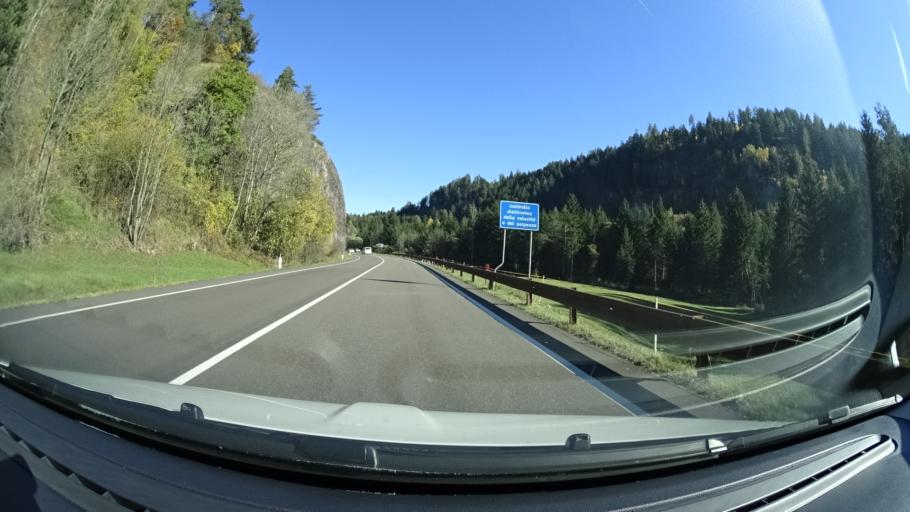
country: IT
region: Trentino-Alto Adige
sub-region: Provincia di Trento
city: Cavalese
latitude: 46.2804
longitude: 11.4565
